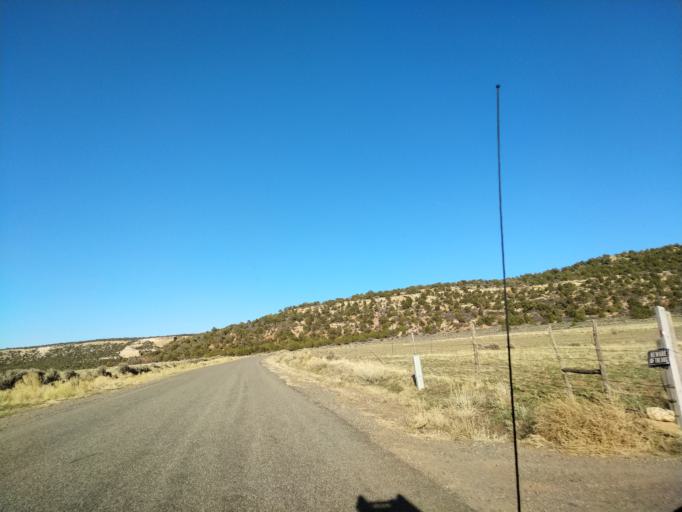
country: US
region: Colorado
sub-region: Mesa County
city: Loma
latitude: 38.9580
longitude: -109.0181
